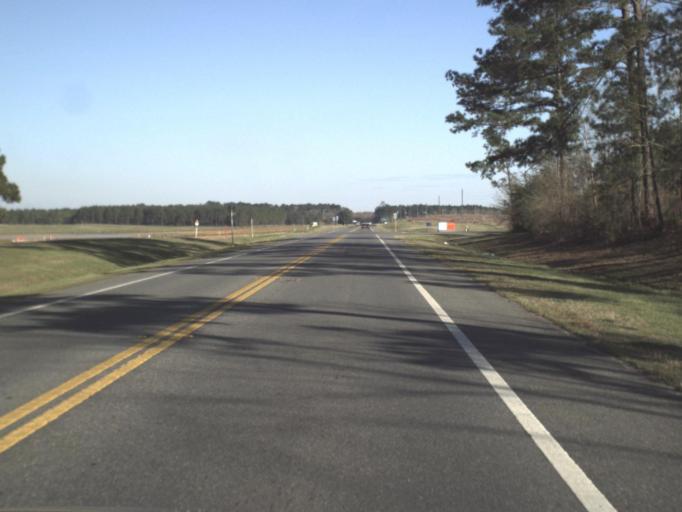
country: US
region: Florida
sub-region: Jackson County
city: Sneads
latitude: 30.7044
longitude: -84.8870
